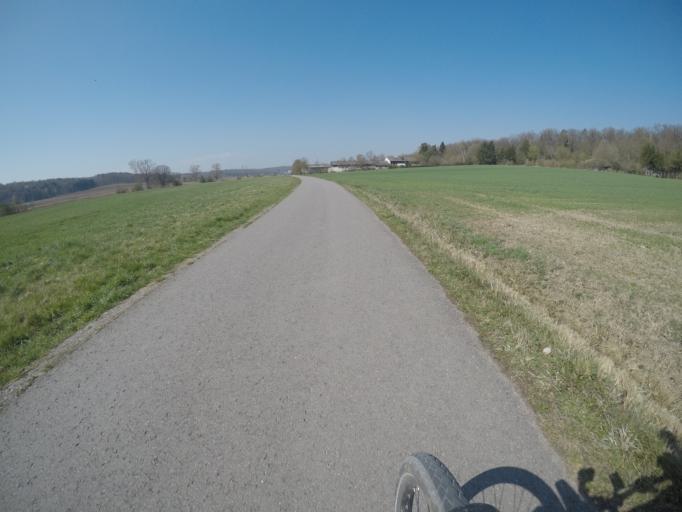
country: DE
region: Baden-Wuerttemberg
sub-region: Regierungsbezirk Stuttgart
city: Magstadt
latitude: 48.7645
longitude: 8.9713
